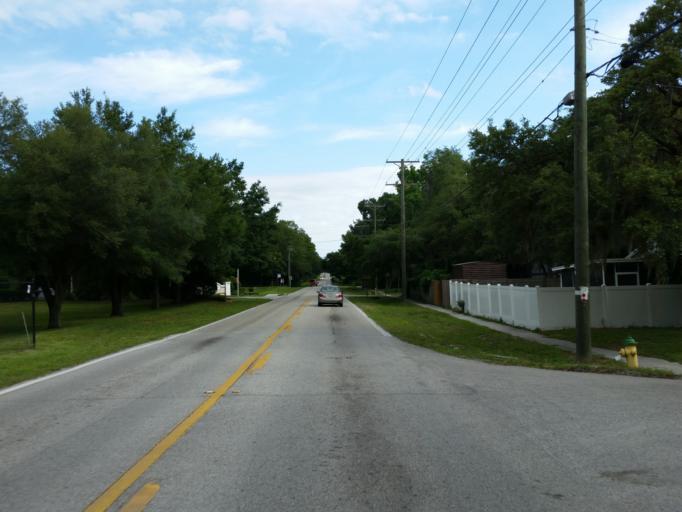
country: US
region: Florida
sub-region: Hillsborough County
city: Riverview
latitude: 27.8811
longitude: -82.3184
